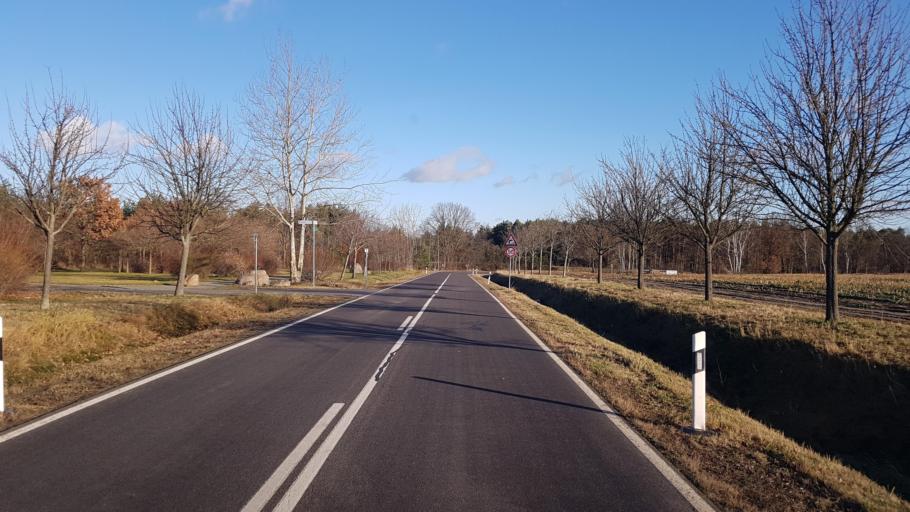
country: DE
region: Brandenburg
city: Forst
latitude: 51.7666
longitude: 14.5696
